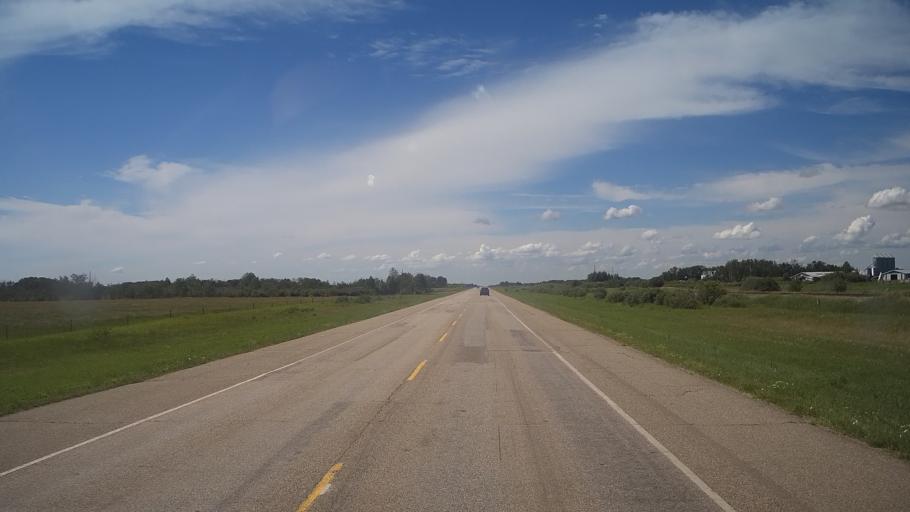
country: CA
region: Saskatchewan
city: Yorkton
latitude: 51.0535
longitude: -102.1893
